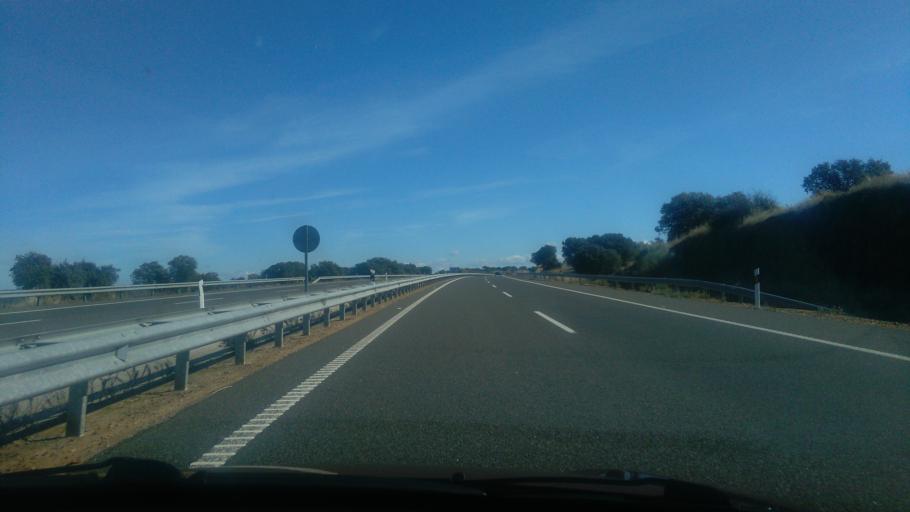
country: ES
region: Extremadura
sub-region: Provincia de Caceres
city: Plasenzuela
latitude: 39.4426
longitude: -6.0430
